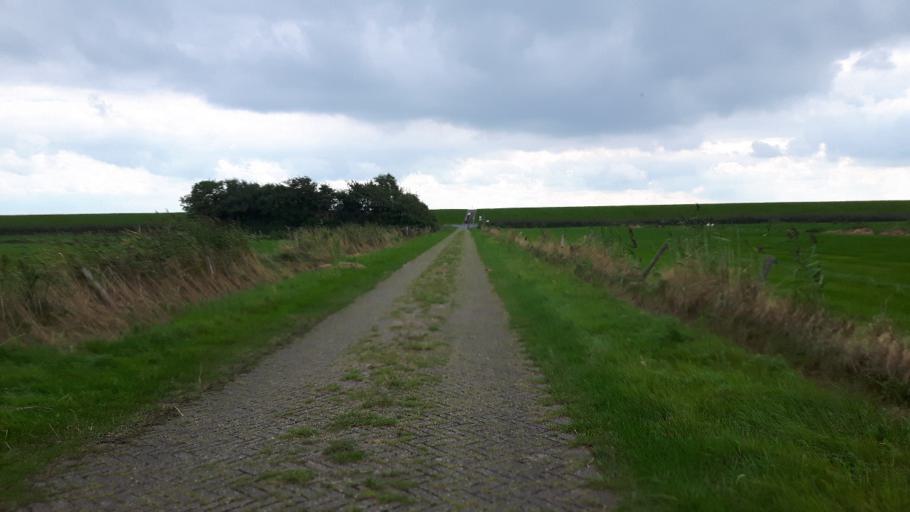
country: NL
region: Friesland
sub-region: Gemeente Ameland
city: Nes
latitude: 53.4442
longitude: 5.8297
